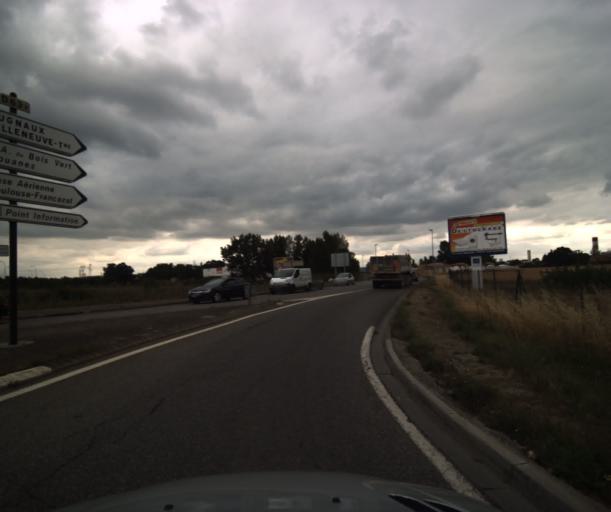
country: FR
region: Midi-Pyrenees
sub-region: Departement de la Haute-Garonne
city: Portet-sur-Garonne
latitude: 43.5379
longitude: 1.3879
